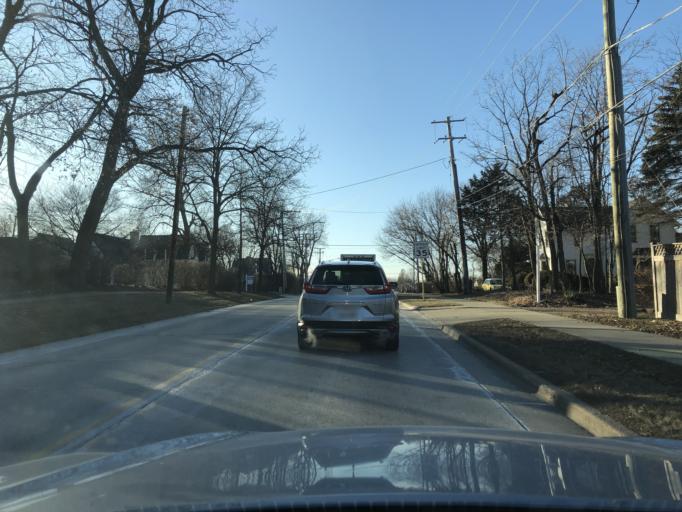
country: US
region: Illinois
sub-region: Cook County
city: Barrington
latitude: 42.1543
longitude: -88.1255
